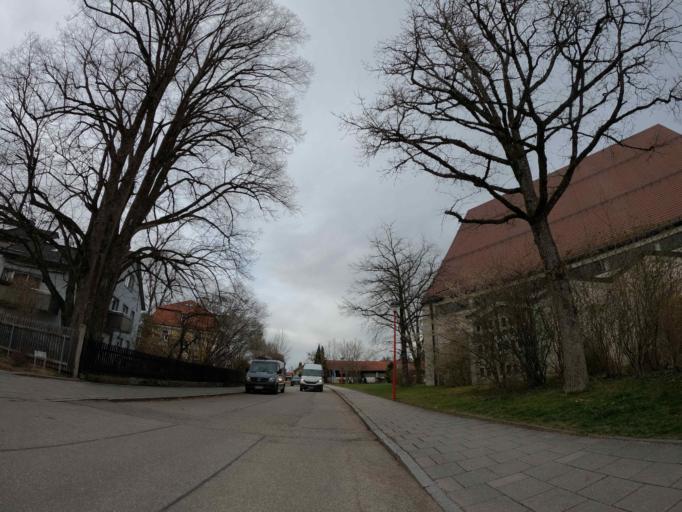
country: DE
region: Bavaria
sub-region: Upper Bavaria
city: Oberhaching
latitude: 48.0204
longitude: 11.5794
